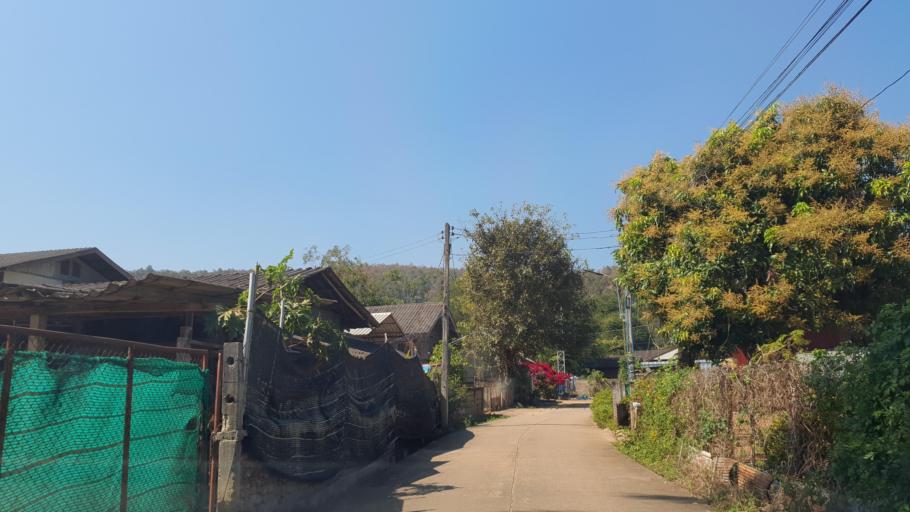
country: TH
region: Lampang
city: Wang Nuea
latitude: 19.1841
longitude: 99.5050
